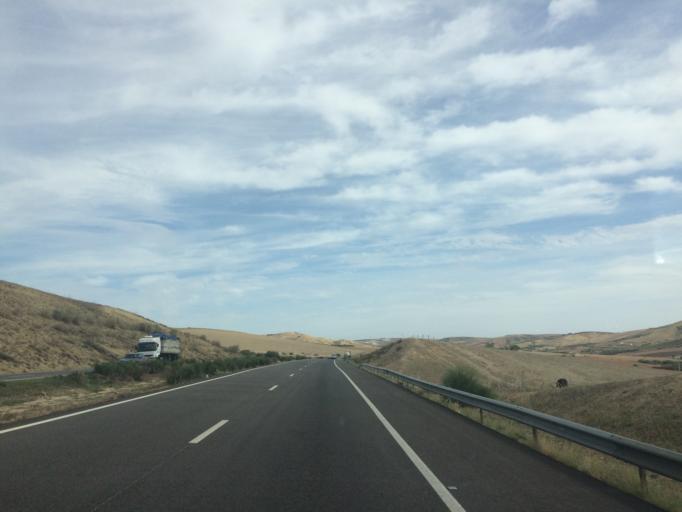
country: MA
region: Rabat-Sale-Zemmour-Zaer
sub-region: Khemisset
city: Khemisset
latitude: 33.8403
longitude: -5.8272
